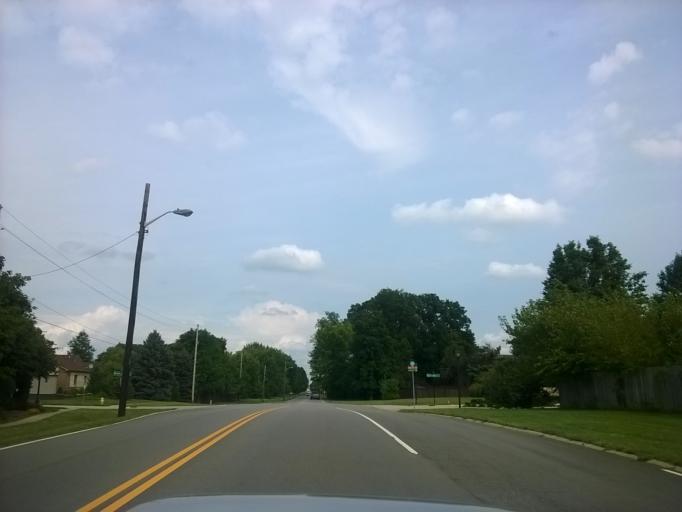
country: US
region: Indiana
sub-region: Hamilton County
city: Carmel
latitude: 39.9785
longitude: -86.0964
